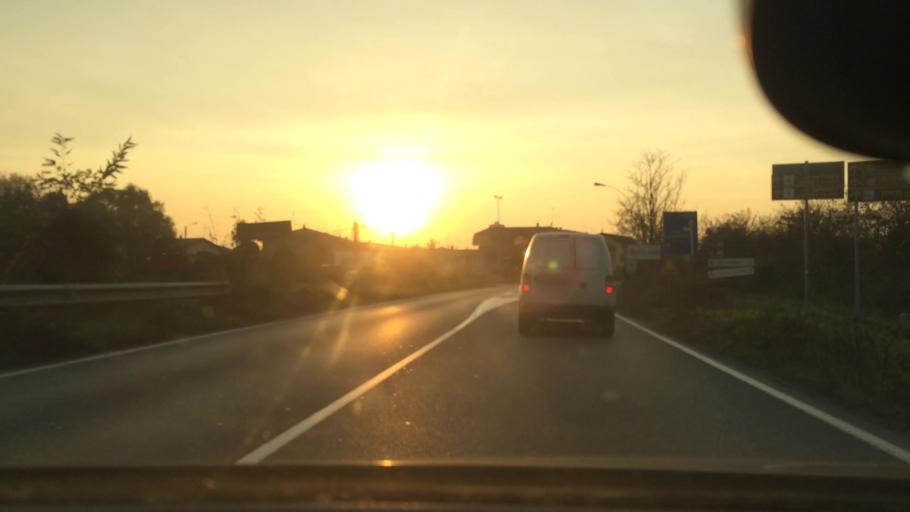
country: IT
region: Lombardy
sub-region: Citta metropolitana di Milano
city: Solaro
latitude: 45.6187
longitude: 9.0915
